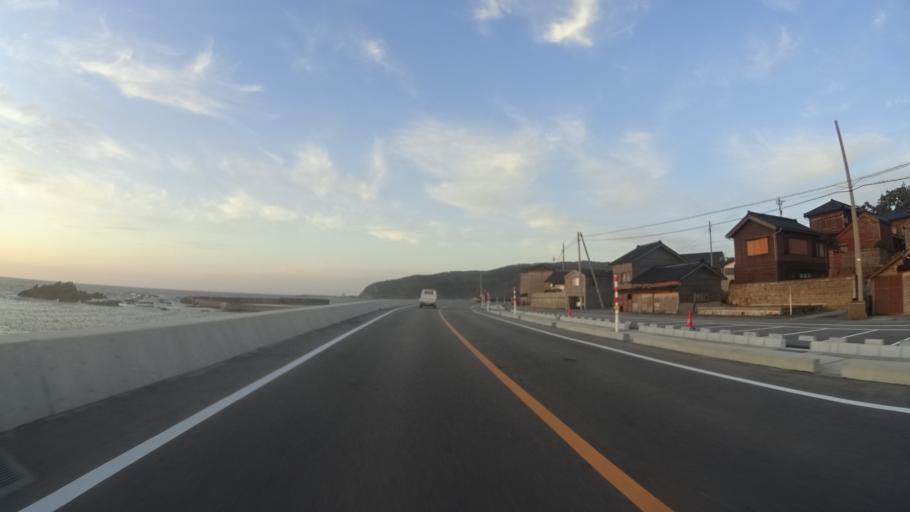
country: JP
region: Ishikawa
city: Nanao
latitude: 37.2804
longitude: 136.7338
